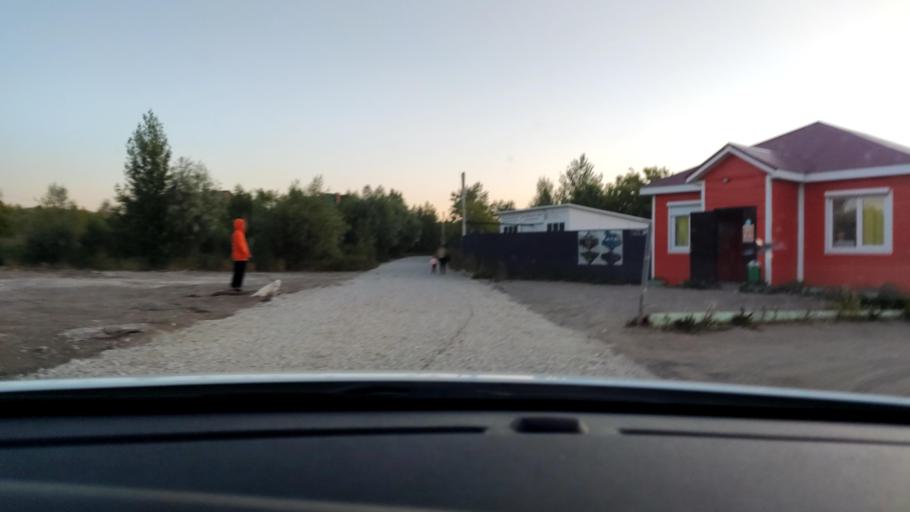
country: RU
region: Tatarstan
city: Stolbishchi
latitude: 55.7379
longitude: 49.2684
